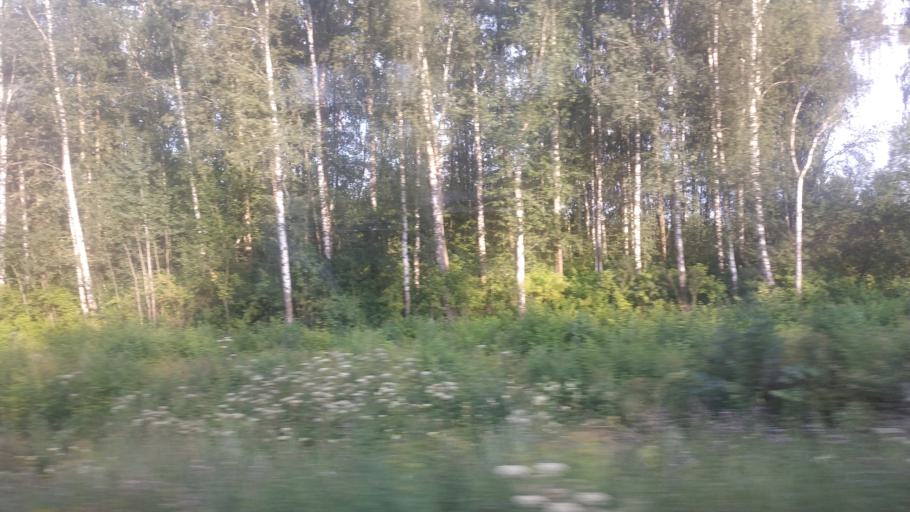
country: RU
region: Moskovskaya
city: Kerva
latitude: 55.5488
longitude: 39.6873
